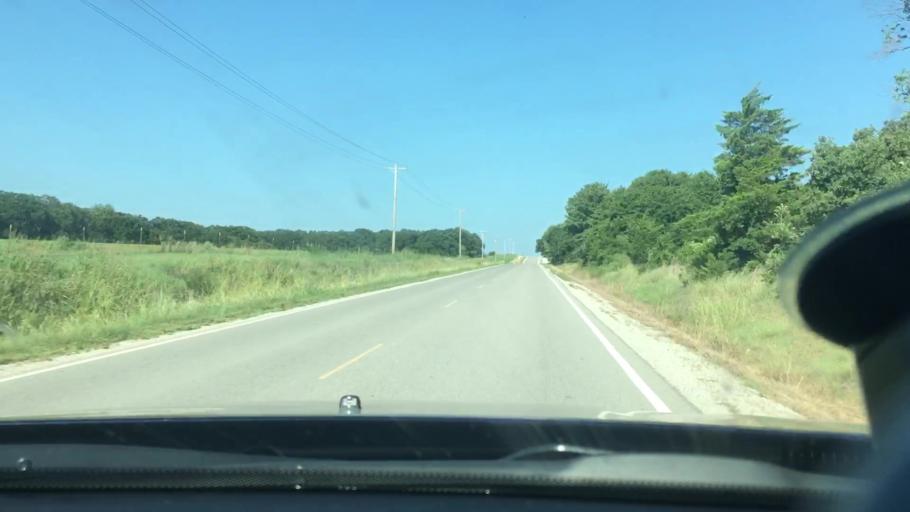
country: US
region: Oklahoma
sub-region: Love County
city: Marietta
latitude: 34.0275
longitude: -97.1918
